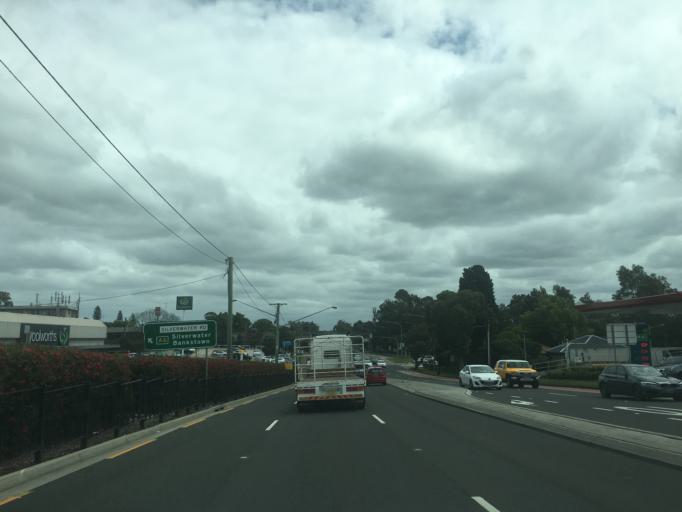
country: AU
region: New South Wales
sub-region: Parramatta
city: Ermington
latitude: -33.8144
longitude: 151.0553
